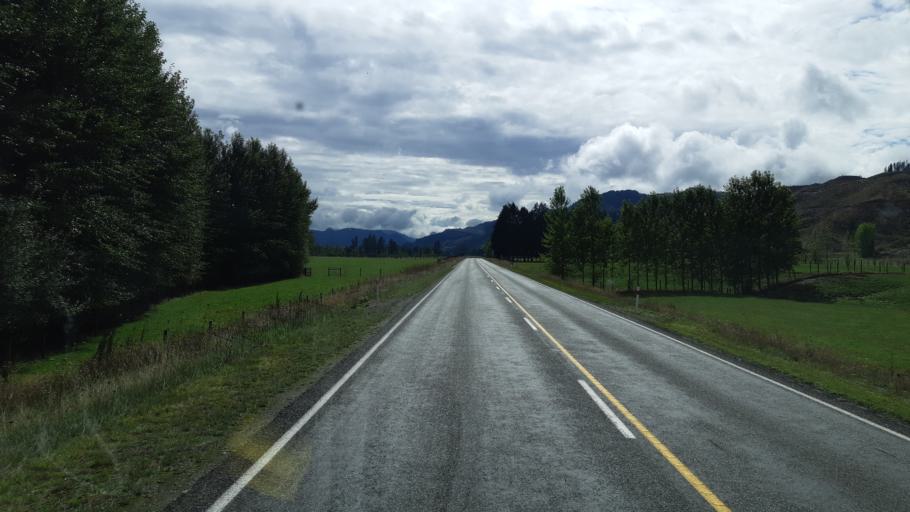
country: NZ
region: West Coast
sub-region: Buller District
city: Westport
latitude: -41.7847
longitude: 172.3703
